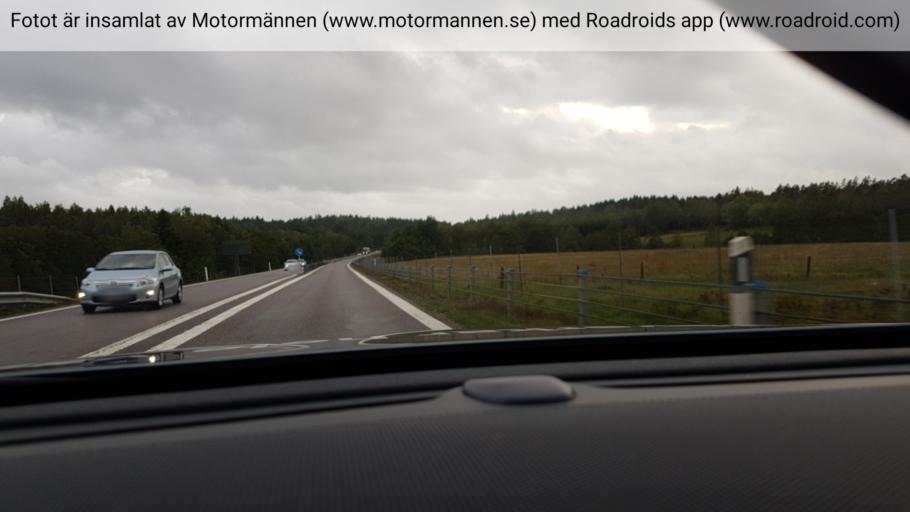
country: SE
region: Vaestra Goetaland
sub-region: Uddevalla Kommun
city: Uddevalla
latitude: 58.3305
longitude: 11.9737
